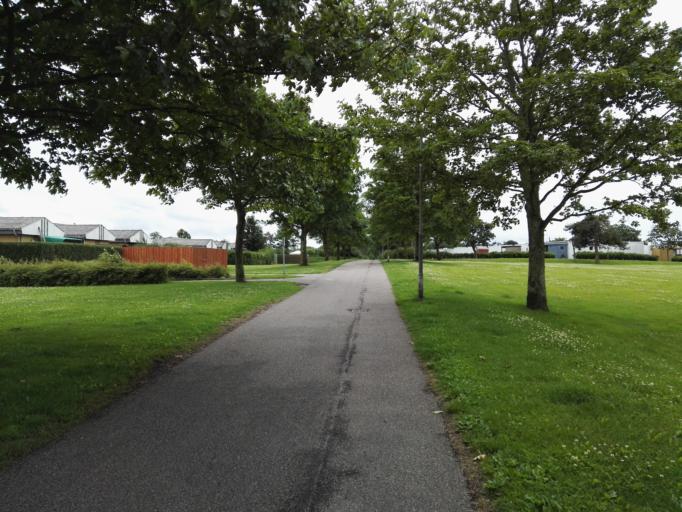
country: DK
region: Capital Region
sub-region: Egedal Kommune
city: Olstykke
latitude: 55.7760
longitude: 12.1674
